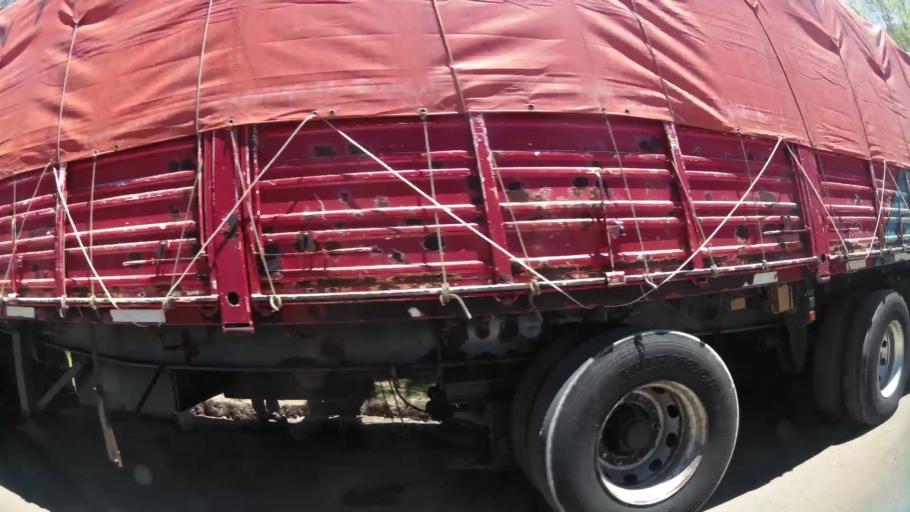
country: AR
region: Santa Fe
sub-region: Departamento de Rosario
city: Rosario
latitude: -32.9601
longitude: -60.7015
